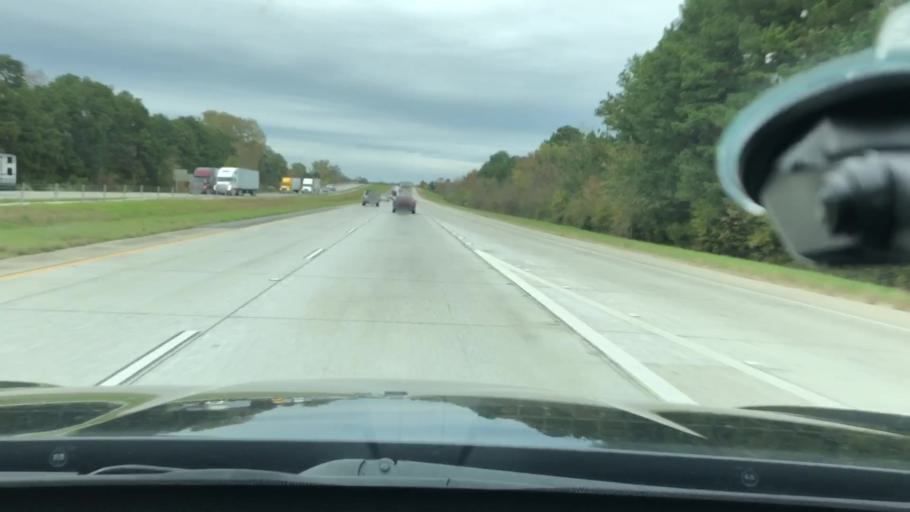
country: US
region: Arkansas
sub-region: Hempstead County
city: Hope
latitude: 33.6125
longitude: -93.7970
